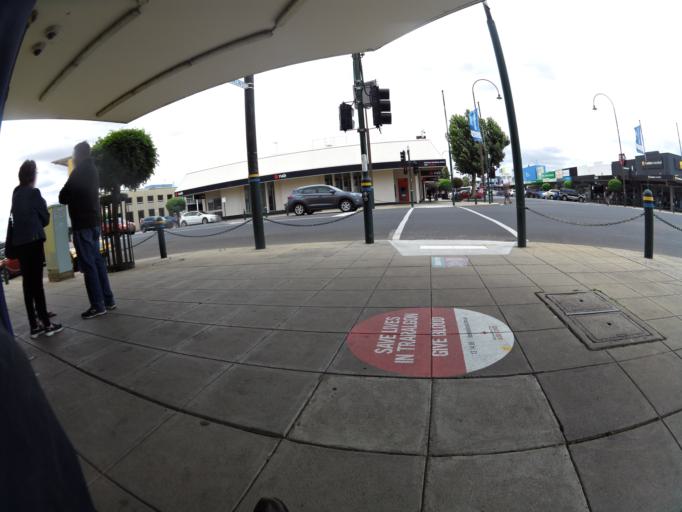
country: AU
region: Victoria
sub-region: Latrobe
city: Traralgon
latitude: -38.1960
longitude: 146.5379
